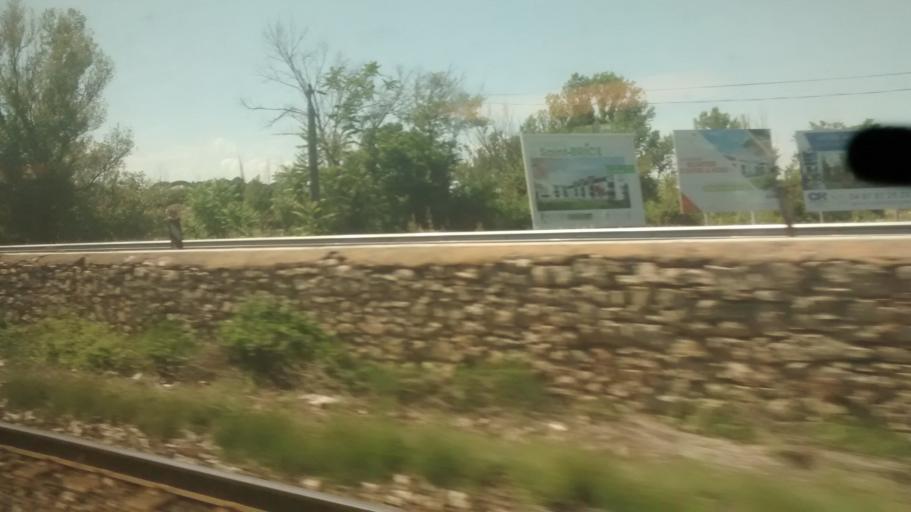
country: FR
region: Languedoc-Roussillon
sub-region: Departement de l'Herault
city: Saint-Bres
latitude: 43.6657
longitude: 4.0413
